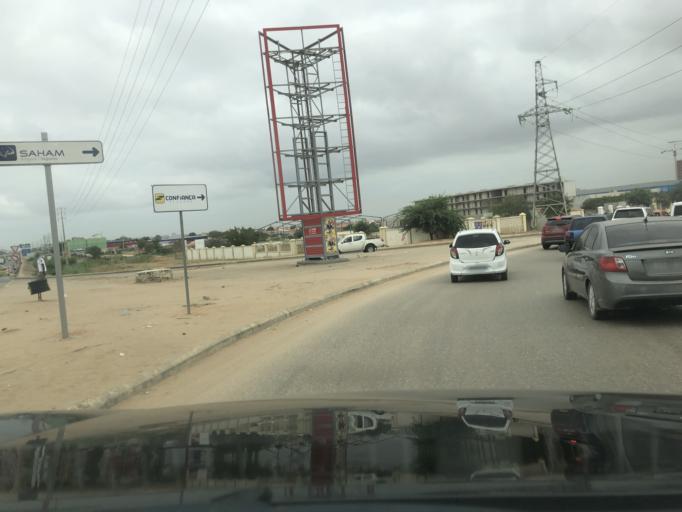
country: AO
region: Luanda
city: Luanda
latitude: -8.9748
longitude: 13.2106
